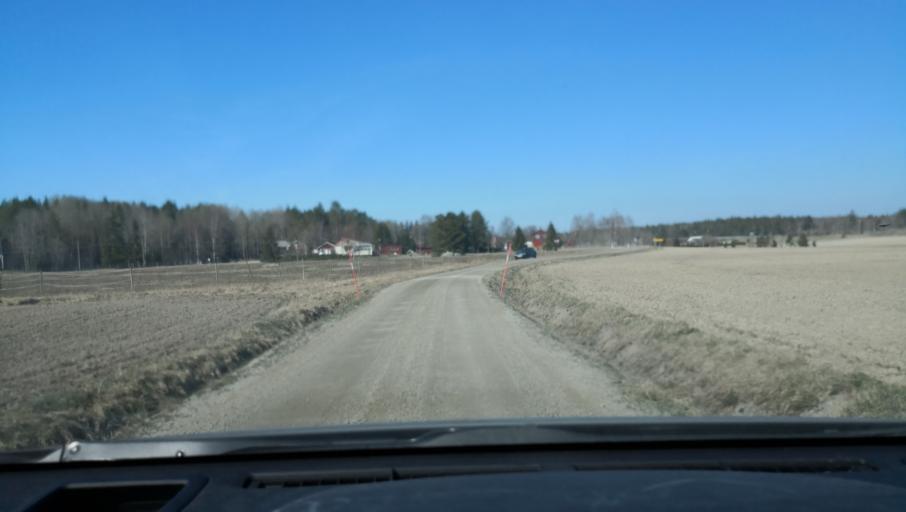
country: SE
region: Vaestmanland
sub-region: Sala Kommun
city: Sala
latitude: 59.9023
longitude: 16.5301
